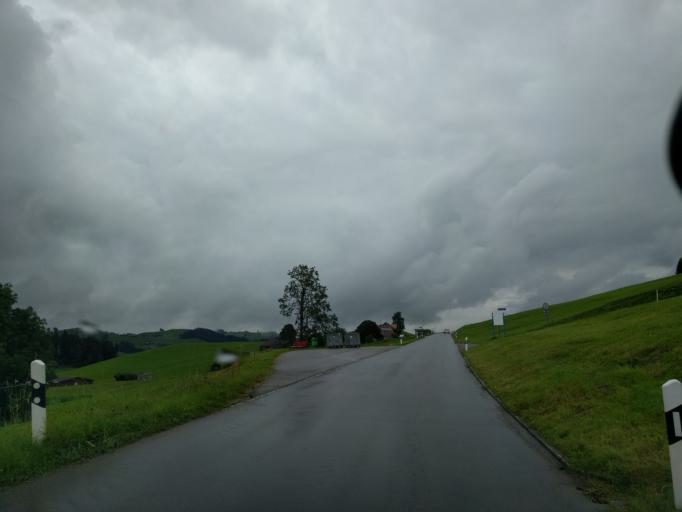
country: CH
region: Saint Gallen
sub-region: Wahlkreis Toggenburg
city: Sankt Peterzell
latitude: 47.3080
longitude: 9.1993
